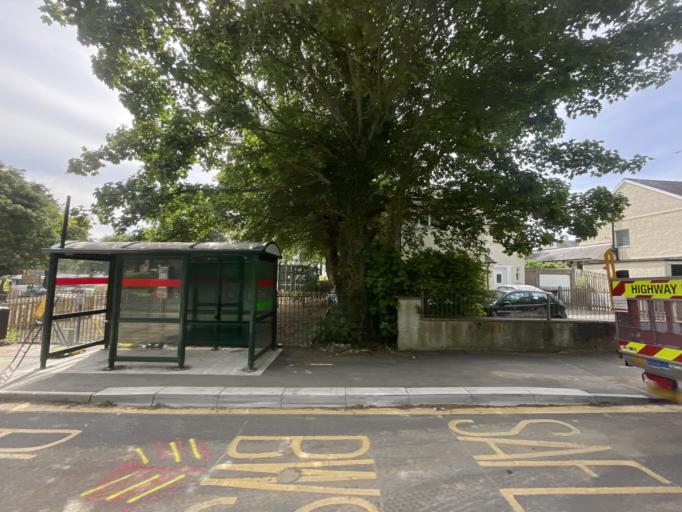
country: GB
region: Wales
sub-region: Gwynedd
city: Bangor
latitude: 53.2230
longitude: -4.1437
